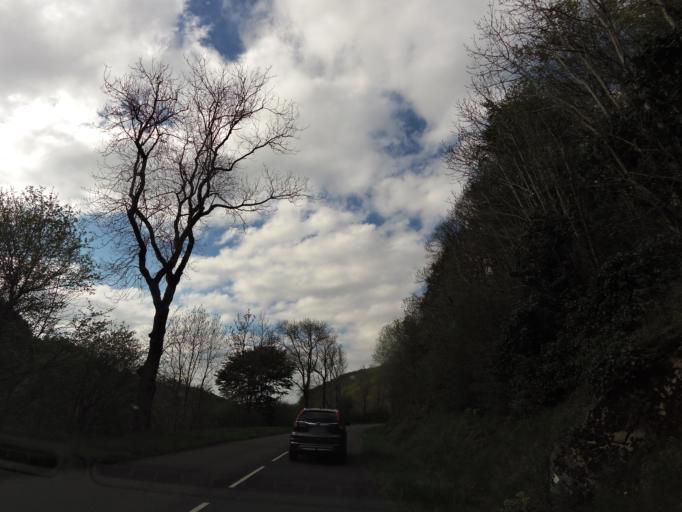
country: FR
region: Midi-Pyrenees
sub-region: Departement du Tarn
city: Soreze
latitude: 43.4200
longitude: 2.0596
